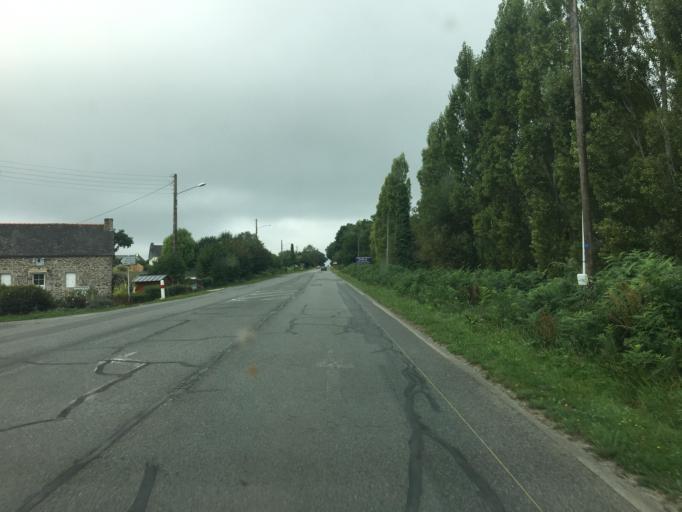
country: FR
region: Brittany
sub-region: Departement des Cotes-d'Armor
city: Gouarec
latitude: 48.2290
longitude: -3.1898
